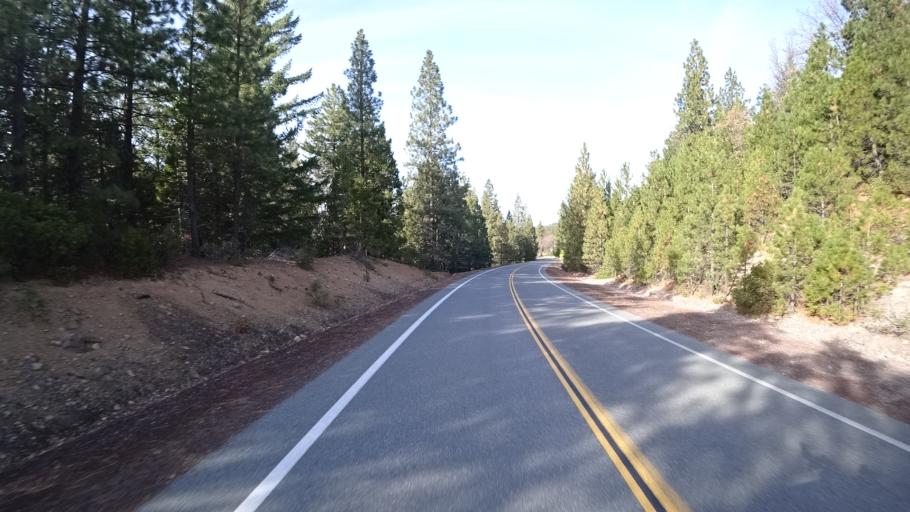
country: US
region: California
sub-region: Siskiyou County
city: Weed
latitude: 41.3914
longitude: -122.4125
